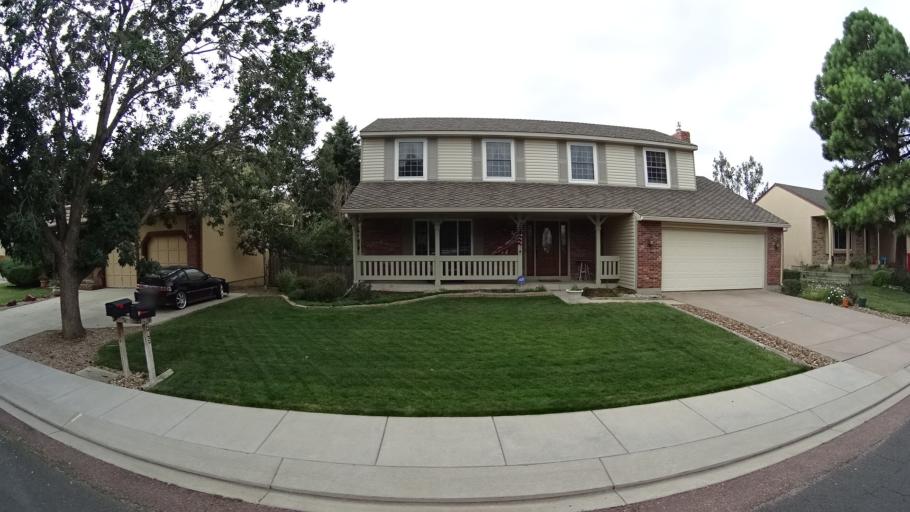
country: US
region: Colorado
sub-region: El Paso County
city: Air Force Academy
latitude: 38.9222
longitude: -104.8332
